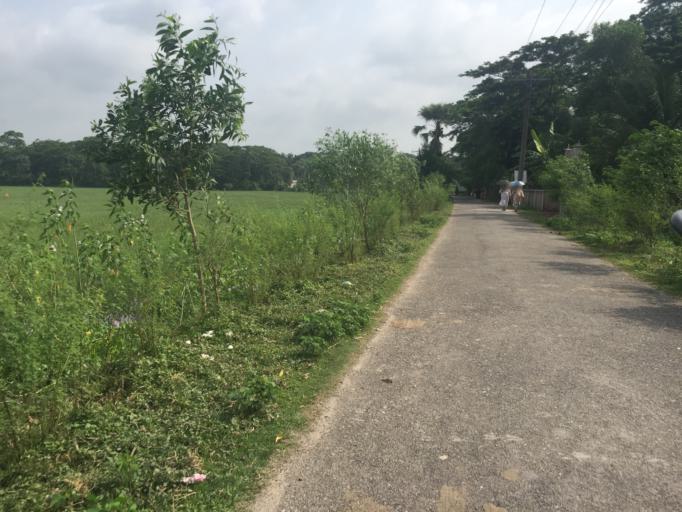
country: BD
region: Barisal
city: Mathba
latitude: 22.2478
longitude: 89.9135
